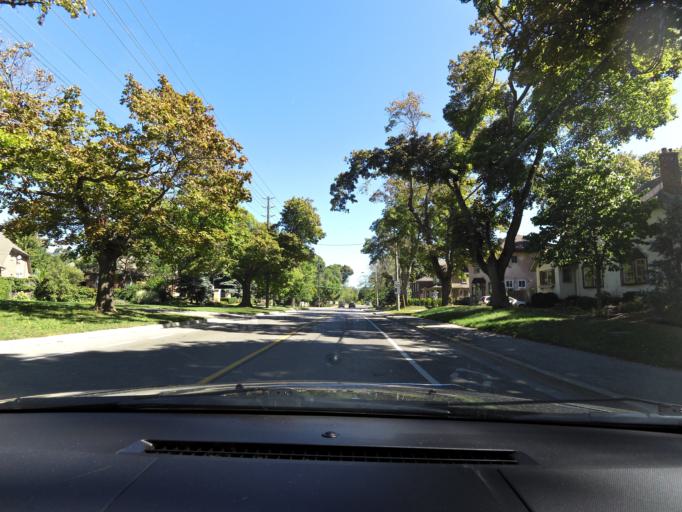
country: CA
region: Ontario
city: Hamilton
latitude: 43.3143
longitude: -79.8135
